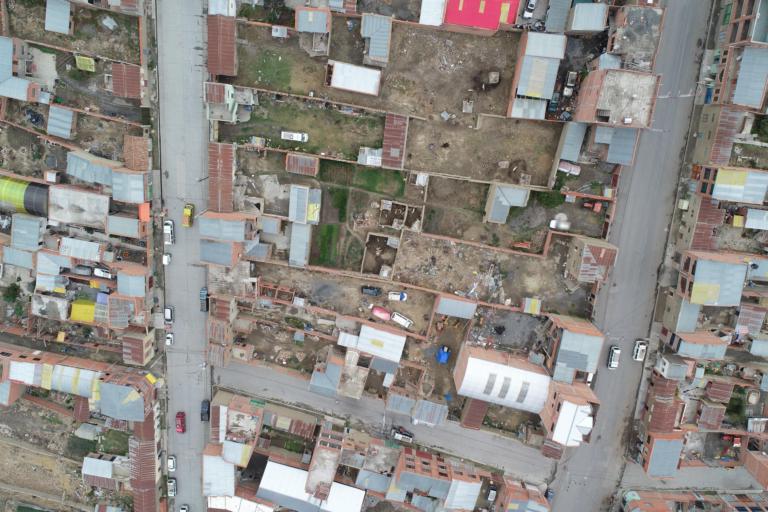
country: BO
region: La Paz
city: Achacachi
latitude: -16.0487
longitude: -68.6824
